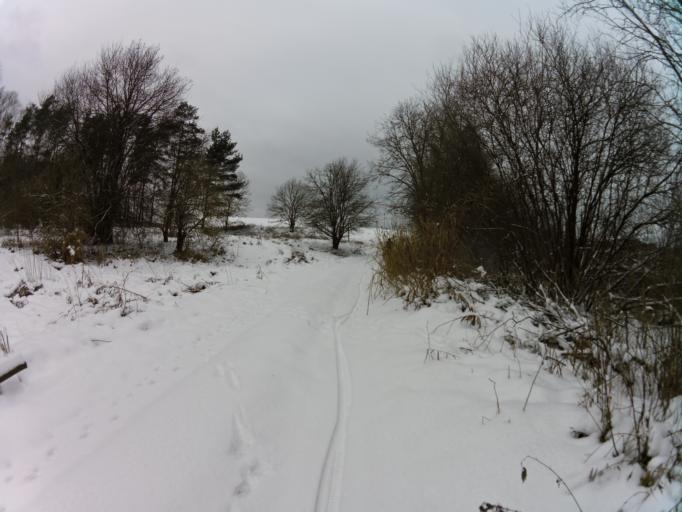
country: PL
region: West Pomeranian Voivodeship
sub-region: Powiat choszczenski
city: Recz
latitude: 53.3349
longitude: 15.5392
